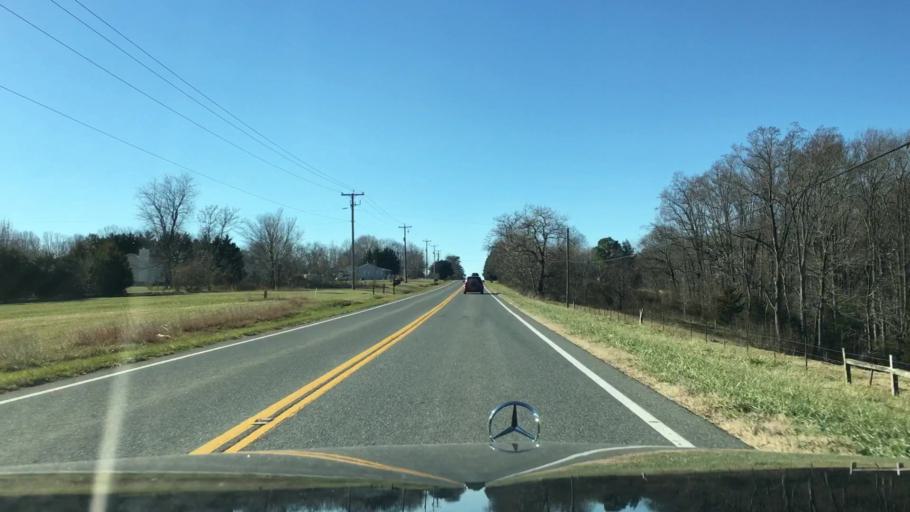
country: US
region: Virginia
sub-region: City of Bedford
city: Bedford
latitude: 37.2397
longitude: -79.6483
